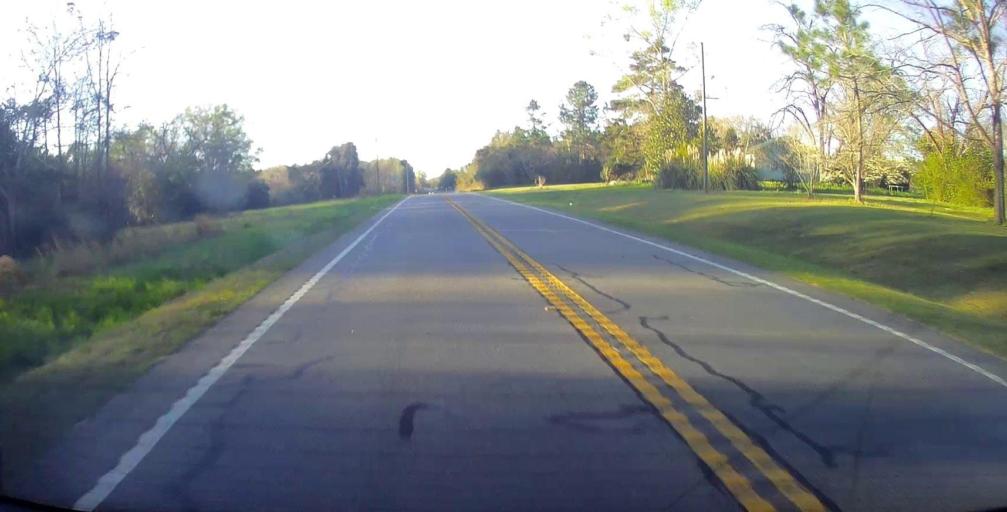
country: US
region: Georgia
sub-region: Wilcox County
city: Abbeville
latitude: 32.0583
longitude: -83.2712
